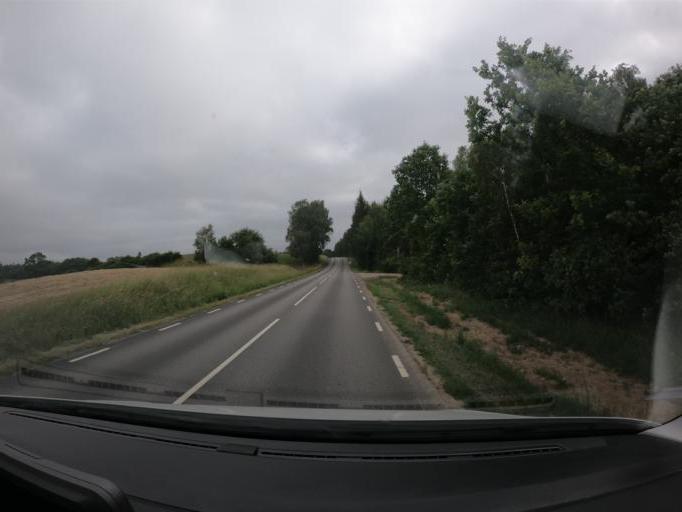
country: SE
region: Skane
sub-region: Perstorps Kommun
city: Perstorp
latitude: 56.0563
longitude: 13.3655
